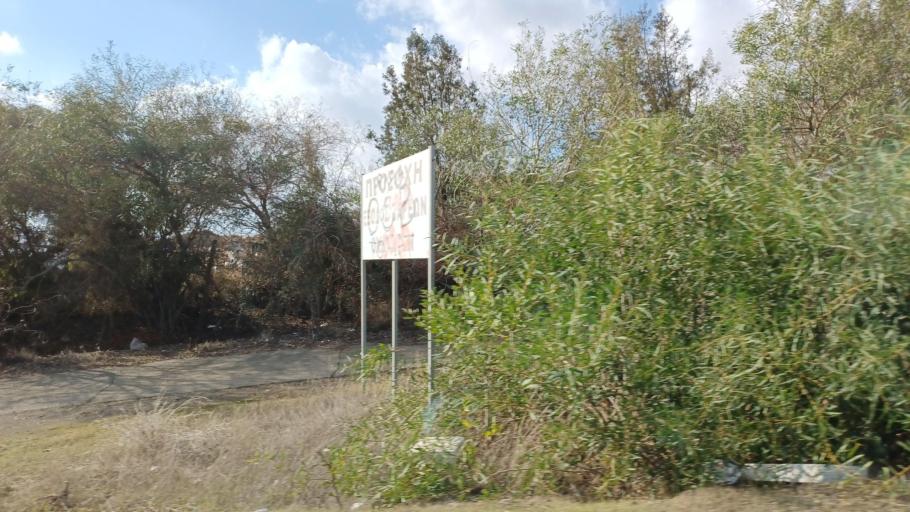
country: CY
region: Larnaka
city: Troulloi
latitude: 35.0162
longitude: 33.6214
